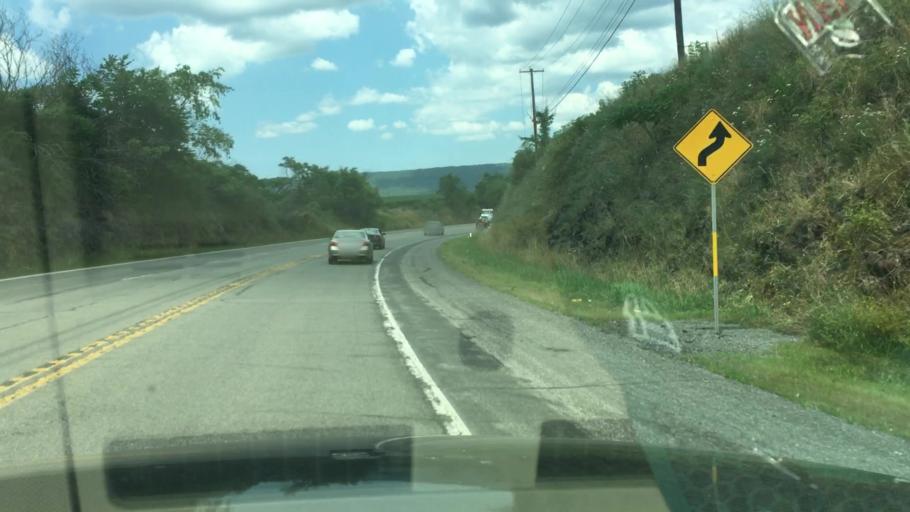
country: US
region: Pennsylvania
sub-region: Northumberland County
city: Mount Carmel
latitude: 40.7331
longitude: -76.3920
